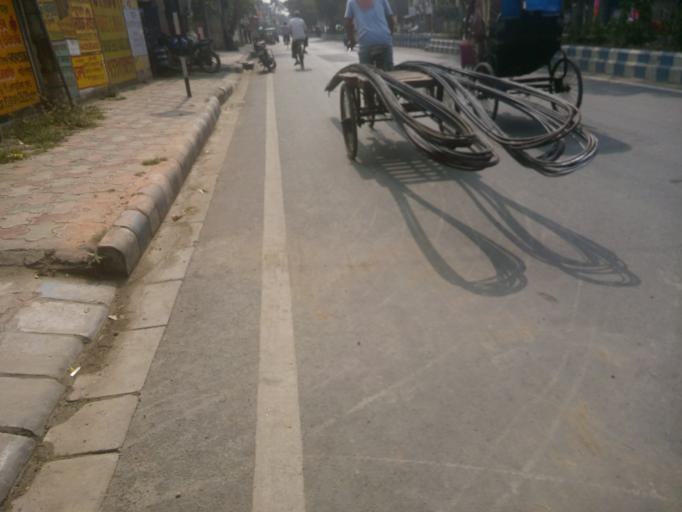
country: IN
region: West Bengal
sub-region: South 24 Paraganas
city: Santoshpur
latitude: 22.4640
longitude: 88.3100
